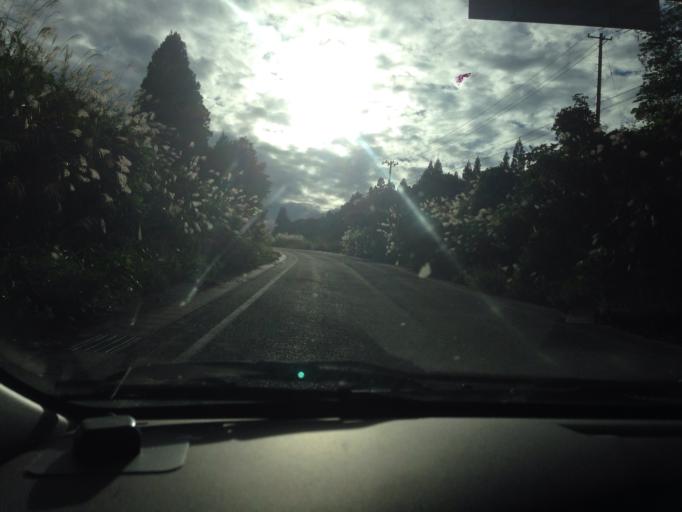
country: JP
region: Fukushima
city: Kitakata
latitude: 37.5990
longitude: 139.7571
